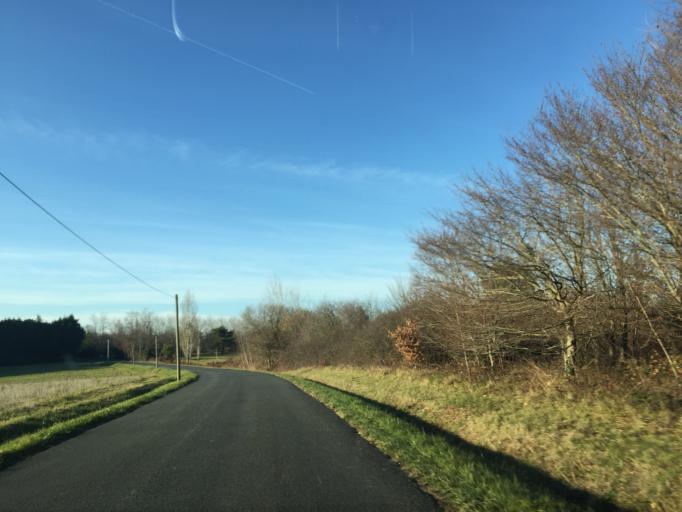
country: FR
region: Aquitaine
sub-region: Departement de la Dordogne
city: Riberac
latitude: 45.2044
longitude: 0.3163
